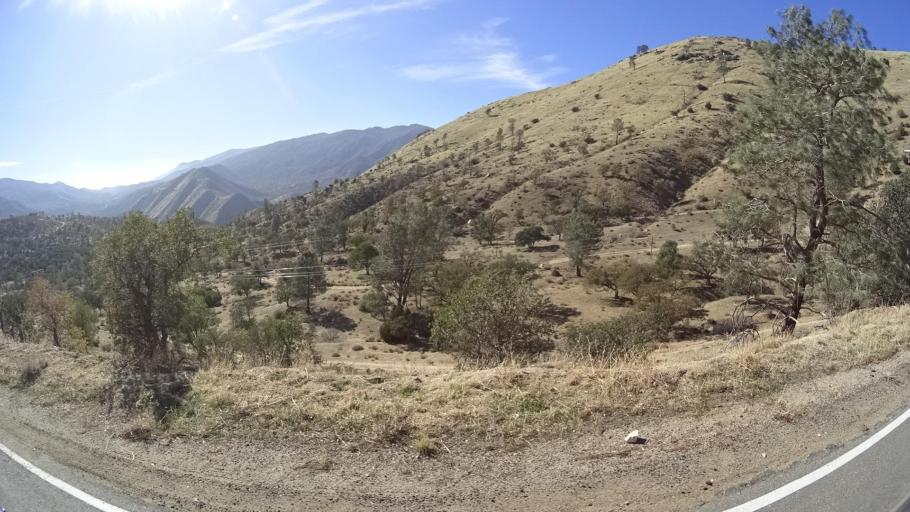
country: US
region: California
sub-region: Kern County
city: Bodfish
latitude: 35.5670
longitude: -118.5058
